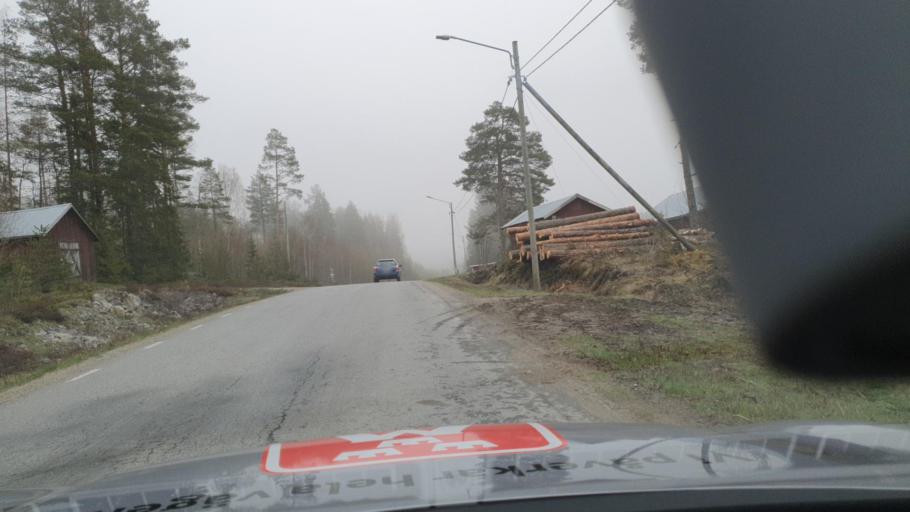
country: SE
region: Vaesternorrland
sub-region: OErnskoeldsviks Kommun
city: Husum
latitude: 63.4874
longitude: 19.1821
